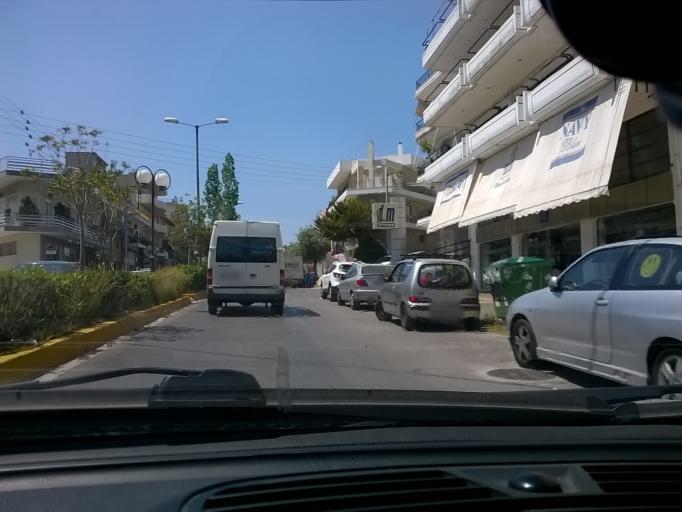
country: GR
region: Attica
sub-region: Nomarchia Athinas
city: Ymittos
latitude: 37.9464
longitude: 23.7574
